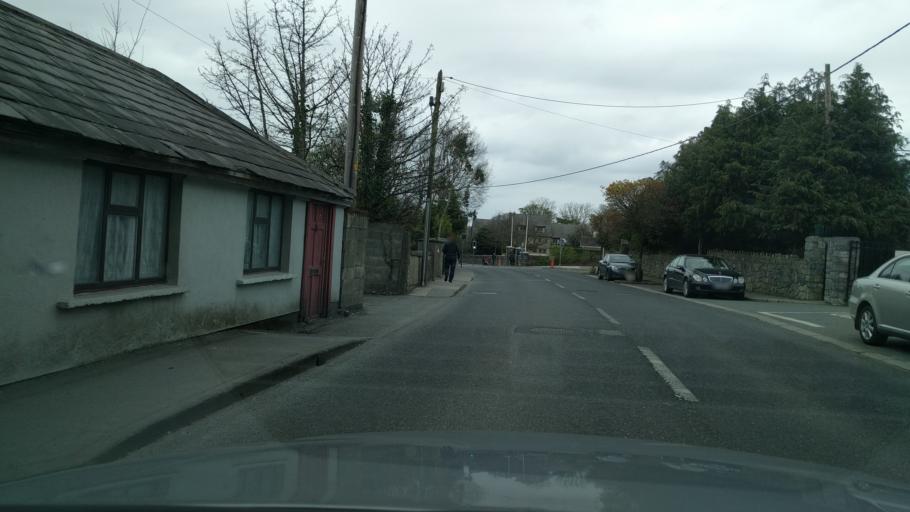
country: IE
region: Leinster
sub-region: South Dublin
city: Saggart
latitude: 53.2809
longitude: -6.4431
